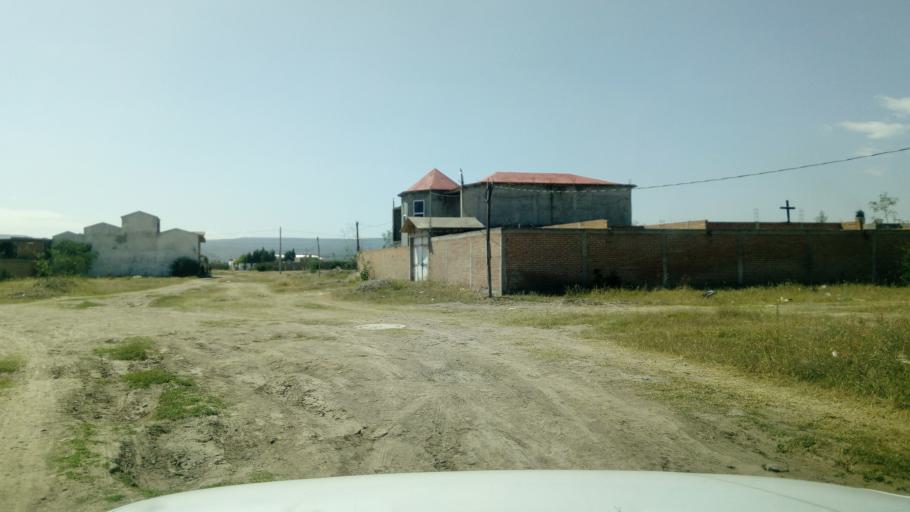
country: MX
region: Durango
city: Victoria de Durango
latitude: 23.9840
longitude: -104.6785
